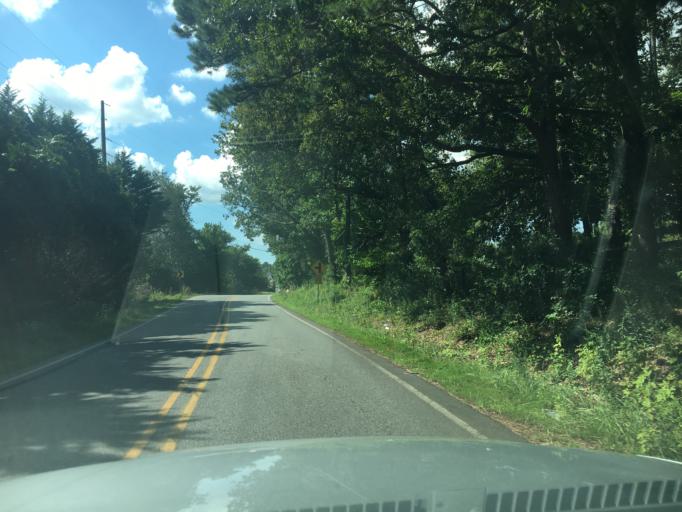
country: US
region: Georgia
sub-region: Cherokee County
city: Holly Springs
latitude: 34.1495
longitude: -84.4660
